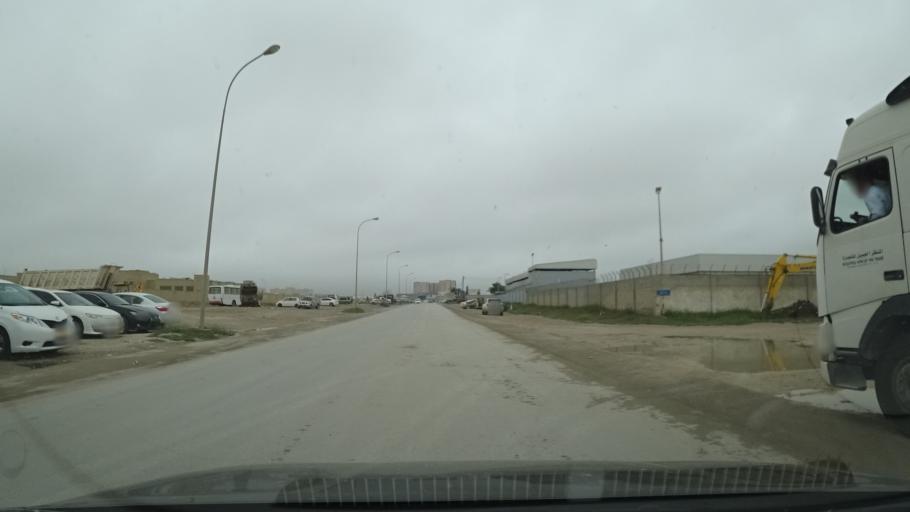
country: OM
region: Zufar
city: Salalah
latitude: 17.0158
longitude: 54.0429
